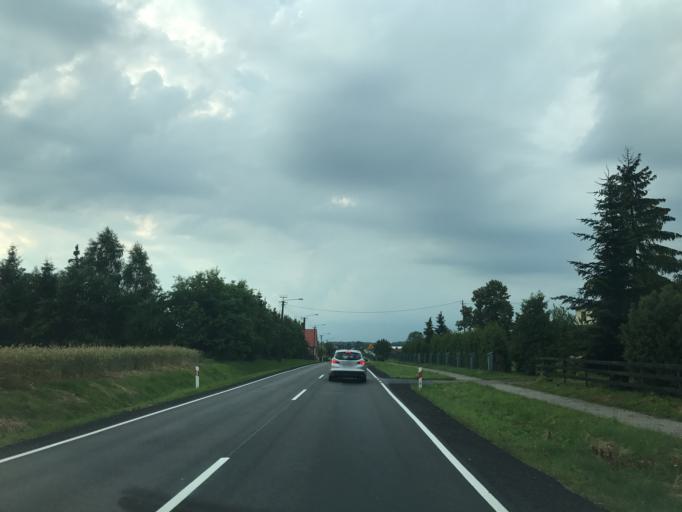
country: PL
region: Pomeranian Voivodeship
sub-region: Powiat czluchowski
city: Czluchow
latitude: 53.6786
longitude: 17.3400
